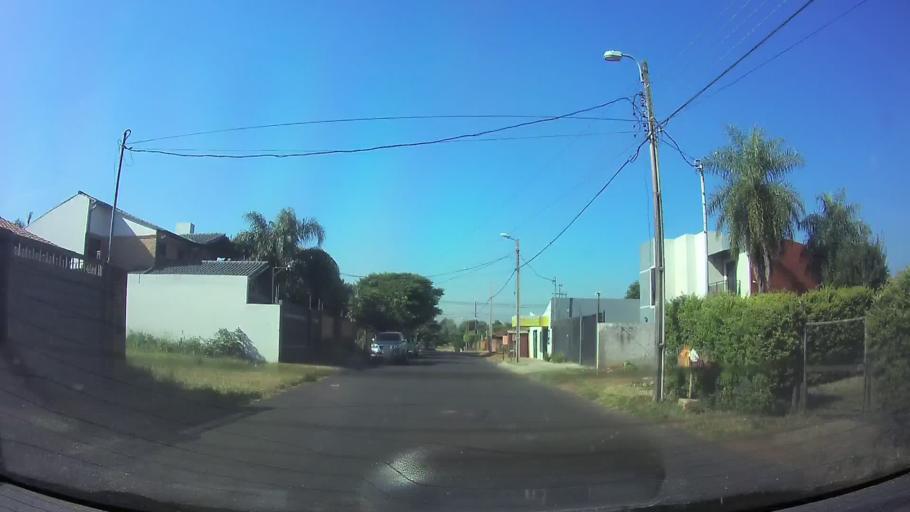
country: PY
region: Central
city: Fernando de la Mora
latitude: -25.2674
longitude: -57.5094
